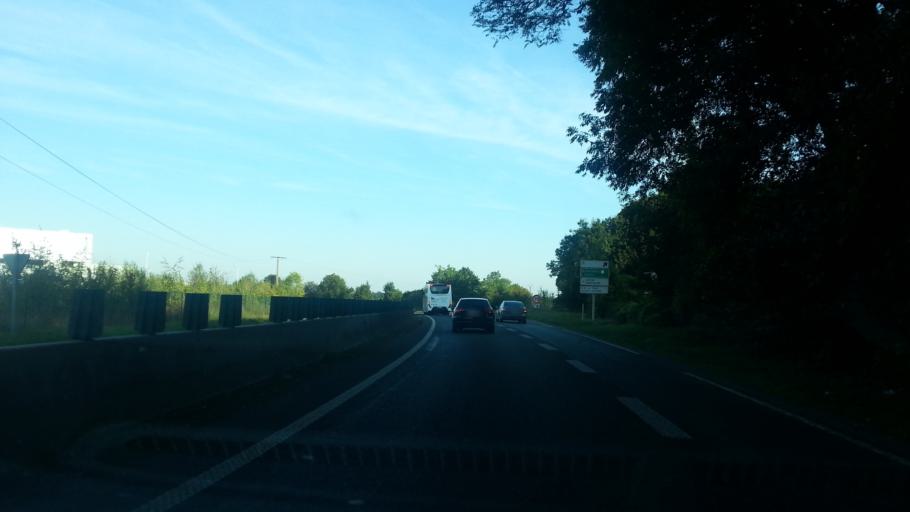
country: FR
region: Picardie
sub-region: Departement de l'Oise
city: Beauvais
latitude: 49.4567
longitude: 2.0685
